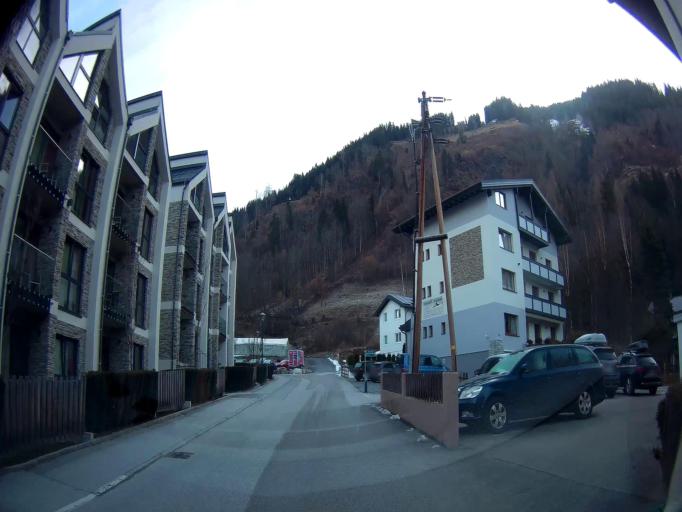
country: AT
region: Salzburg
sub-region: Politischer Bezirk Sankt Johann im Pongau
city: Dorfgastein
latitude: 47.2419
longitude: 13.1092
